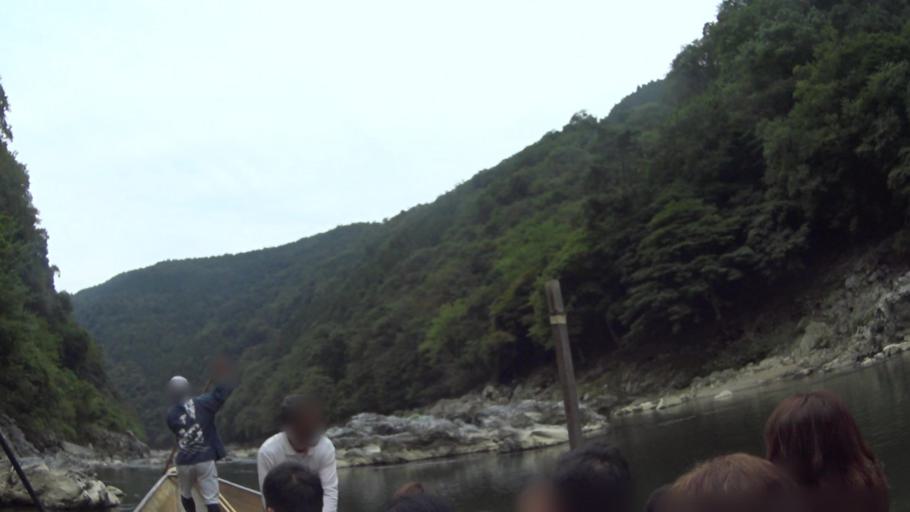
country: JP
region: Kyoto
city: Muko
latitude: 35.0210
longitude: 135.6567
